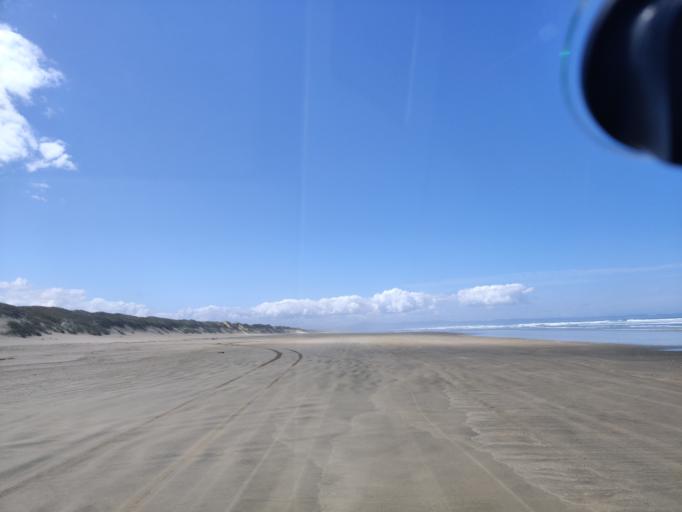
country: NZ
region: Northland
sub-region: Far North District
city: Kaitaia
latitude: -34.9418
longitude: 173.1160
